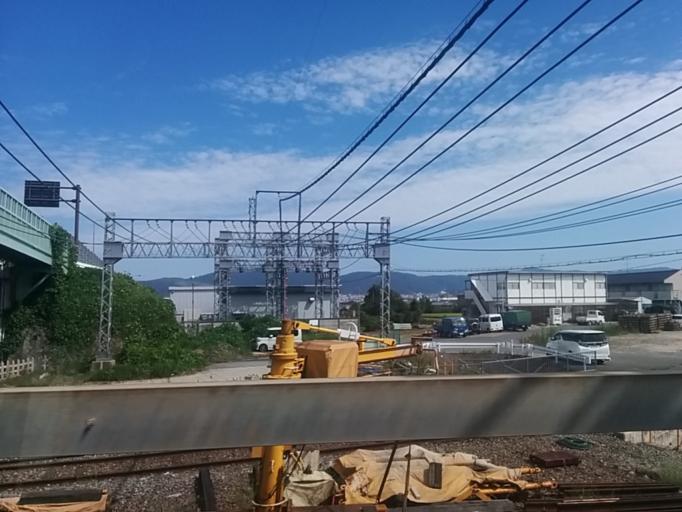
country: JP
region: Nara
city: Nara-shi
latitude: 34.6837
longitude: 135.7837
